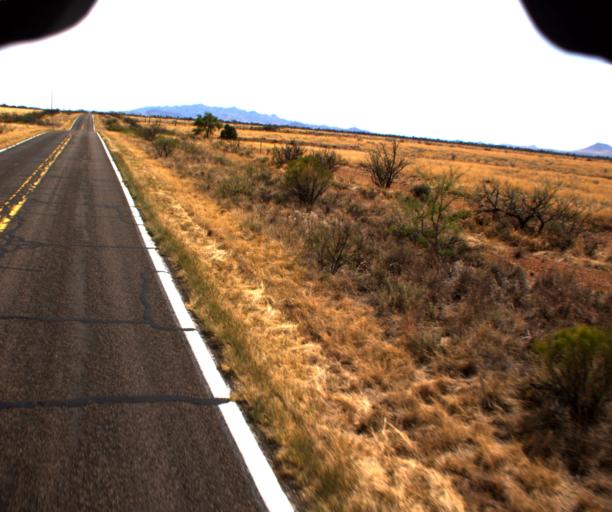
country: US
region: Arizona
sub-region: Cochise County
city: Willcox
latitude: 31.9075
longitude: -109.4914
